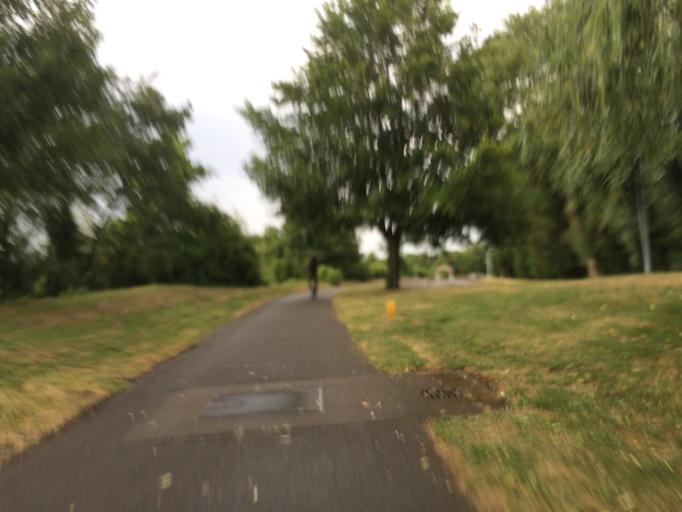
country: FR
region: Picardie
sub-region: Departement de l'Oise
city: Venette
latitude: 49.4110
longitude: 2.8000
